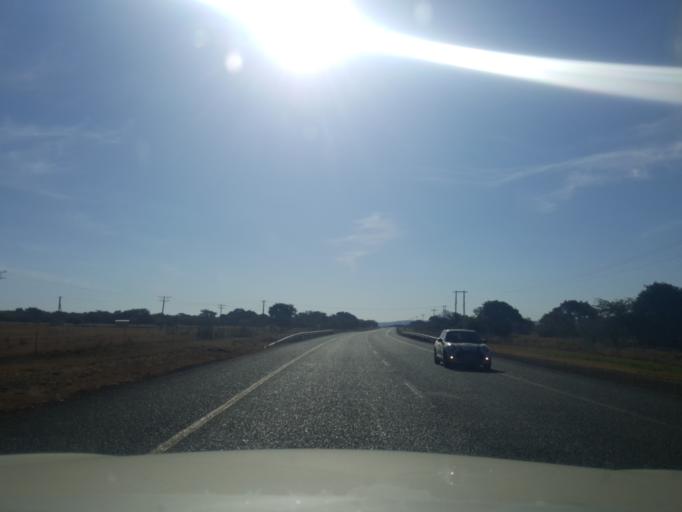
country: ZA
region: North-West
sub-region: Ngaka Modiri Molema District Municipality
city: Zeerust
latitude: -25.5521
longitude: 26.2095
